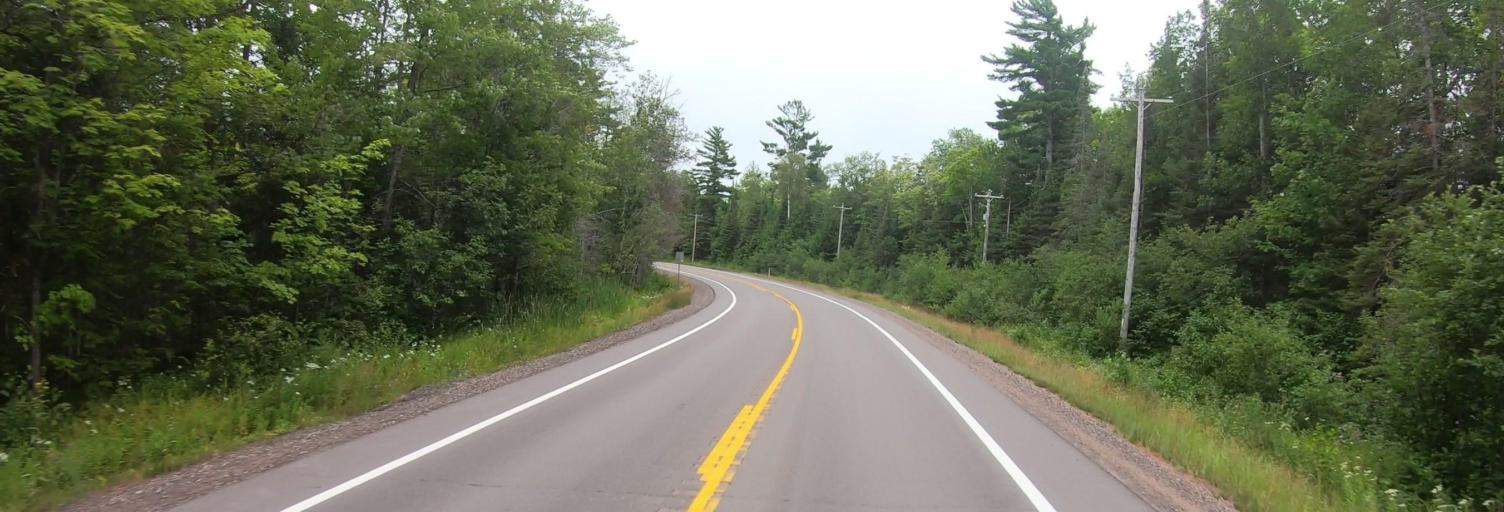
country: US
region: Michigan
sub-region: Keweenaw County
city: Eagle River
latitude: 47.3967
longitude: -88.2841
